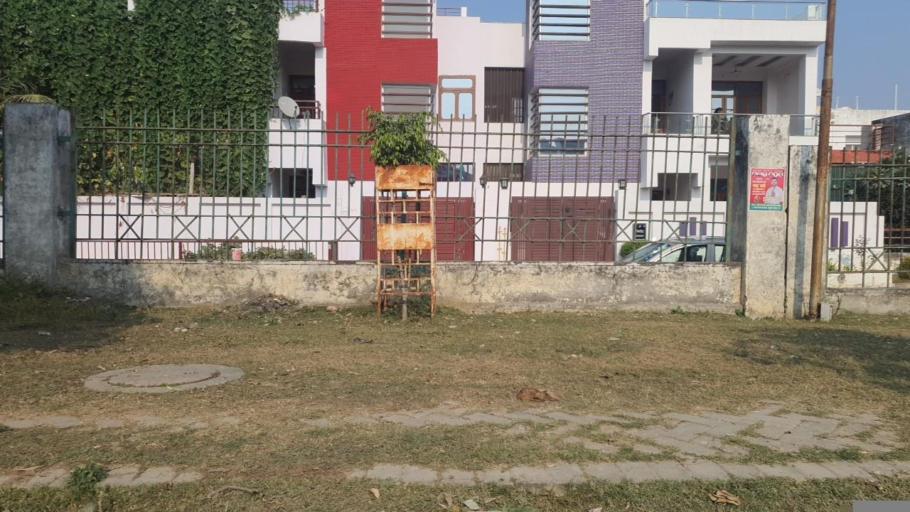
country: IN
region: Uttar Pradesh
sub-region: Lucknow District
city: Lucknow
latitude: 26.7956
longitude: 81.0078
